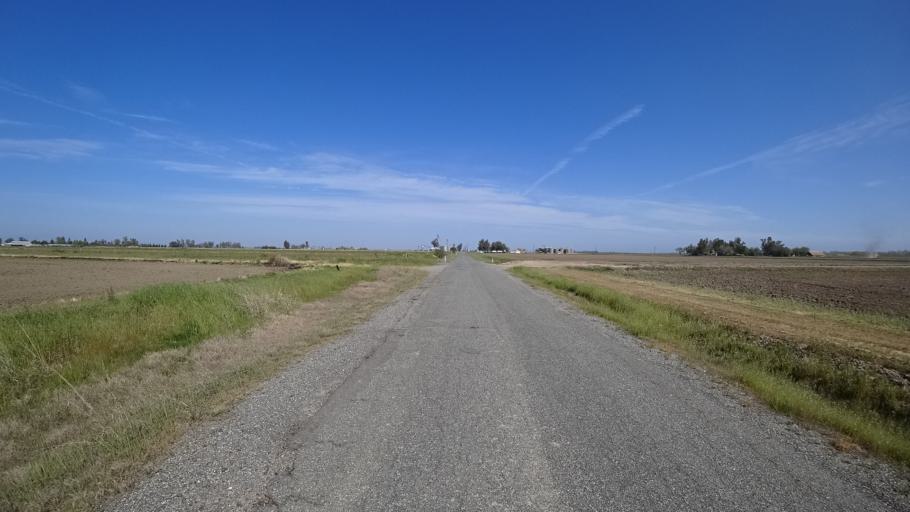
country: US
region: California
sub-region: Glenn County
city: Hamilton City
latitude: 39.5756
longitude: -122.0277
